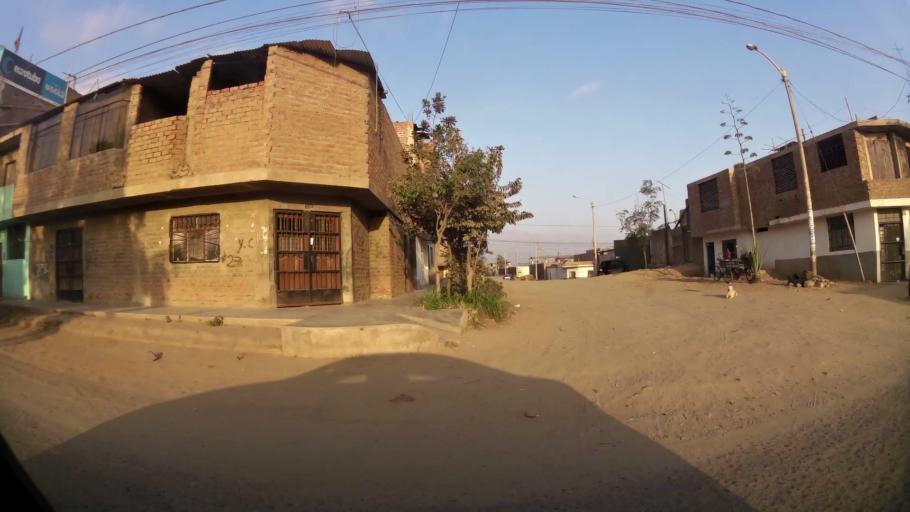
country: PE
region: La Libertad
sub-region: Provincia de Trujillo
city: El Porvenir
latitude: -8.0697
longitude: -78.9930
